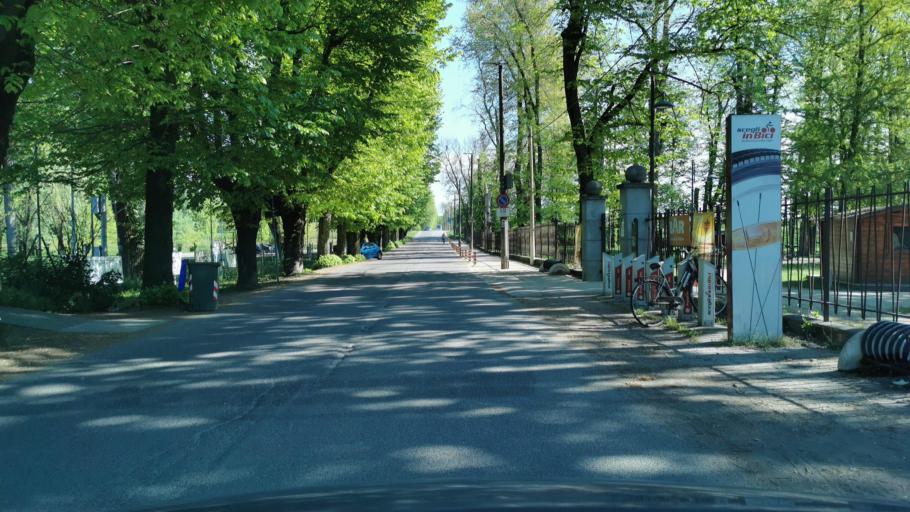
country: IT
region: Lombardy
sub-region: Provincia di Cremona
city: Cremona
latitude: 45.1233
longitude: 10.0057
